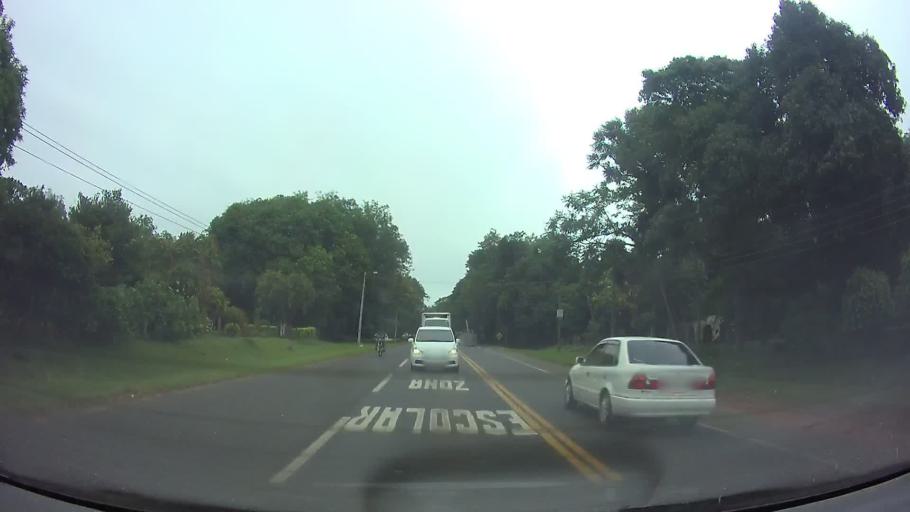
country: PY
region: Paraguari
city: Yaguaron
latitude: -25.5906
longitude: -57.2275
